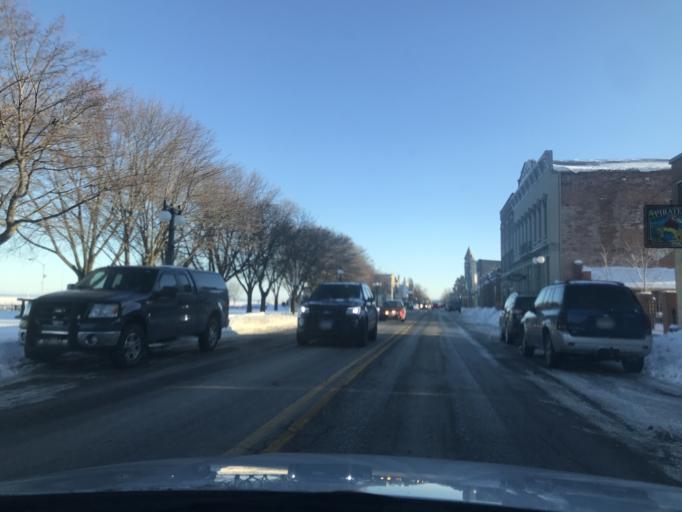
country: US
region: Michigan
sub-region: Menominee County
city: Menominee
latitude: 45.1057
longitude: -87.6039
